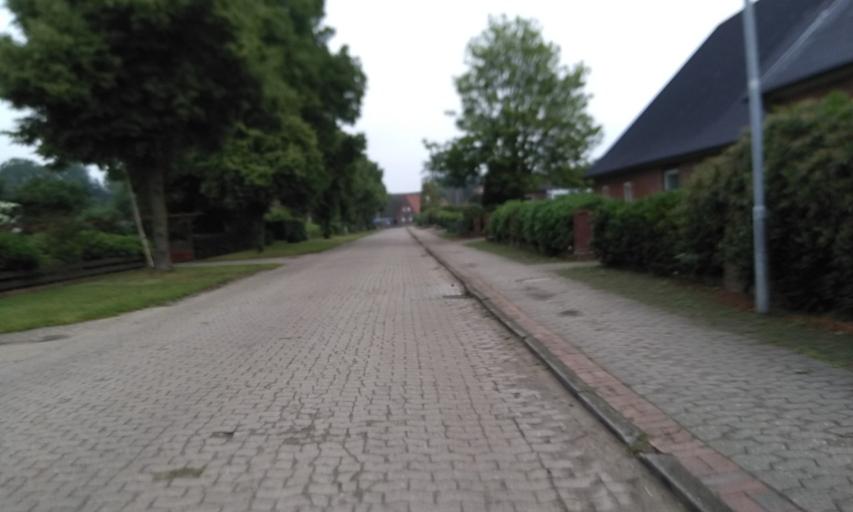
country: DE
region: Lower Saxony
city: Deinste
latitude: 53.5248
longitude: 9.4433
